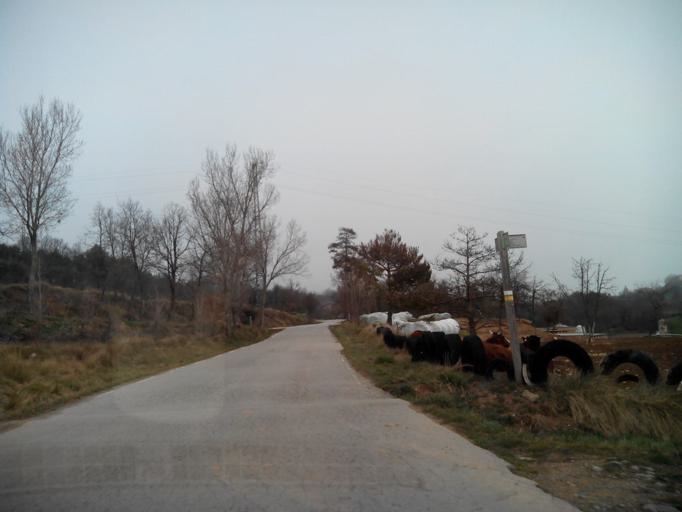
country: ES
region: Catalonia
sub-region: Provincia de Barcelona
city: Olost
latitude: 41.9821
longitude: 2.1613
